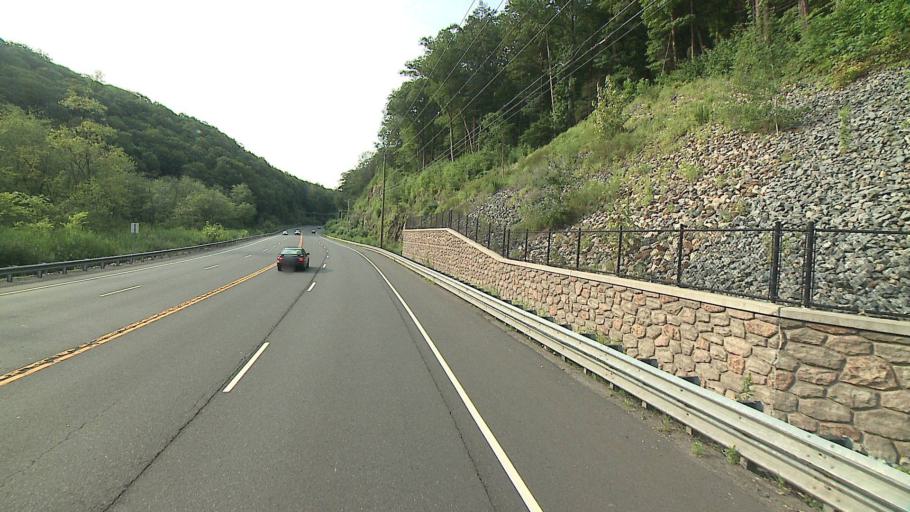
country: US
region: Connecticut
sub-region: Fairfield County
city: Danbury
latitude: 41.3573
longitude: -73.4716
